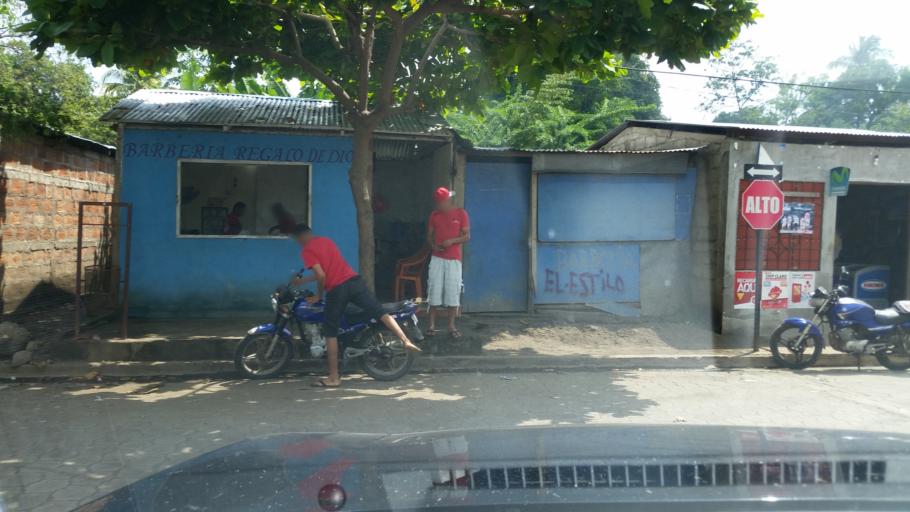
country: NI
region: Chinandega
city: Puerto Morazan
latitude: 12.7682
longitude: -87.1359
